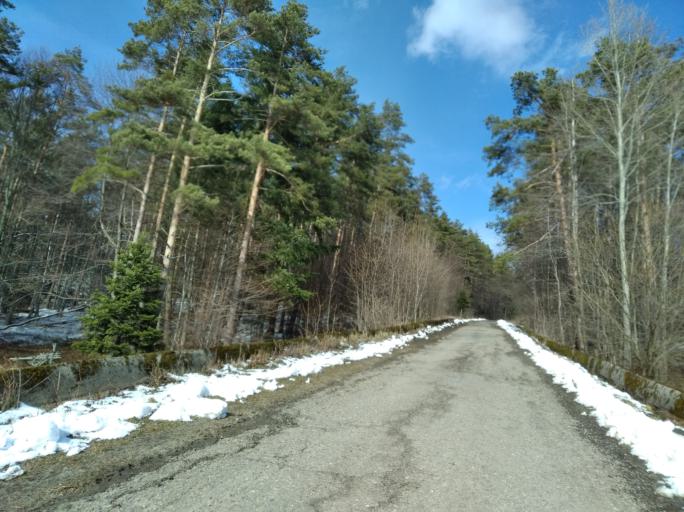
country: PL
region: Subcarpathian Voivodeship
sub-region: Powiat krosnienski
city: Korczyna
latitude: 49.7511
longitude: 21.8148
